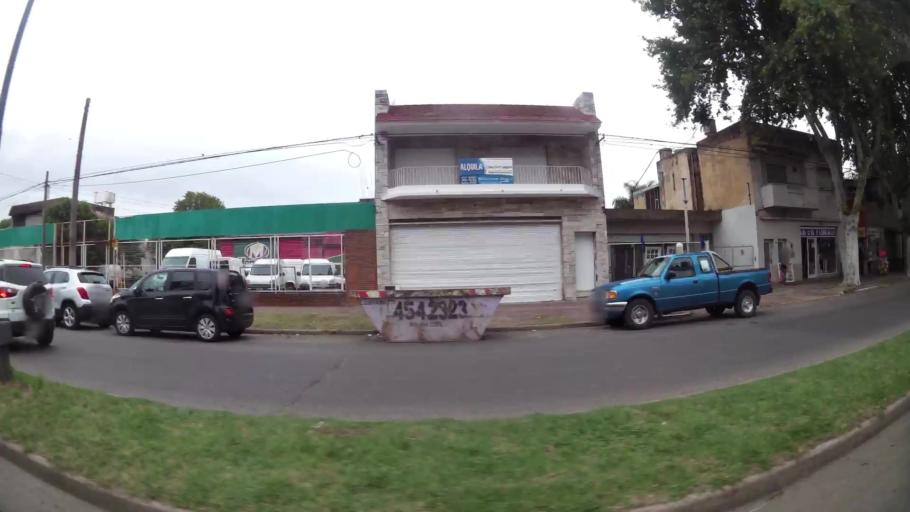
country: AR
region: Santa Fe
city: Granadero Baigorria
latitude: -32.8776
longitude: -60.6975
